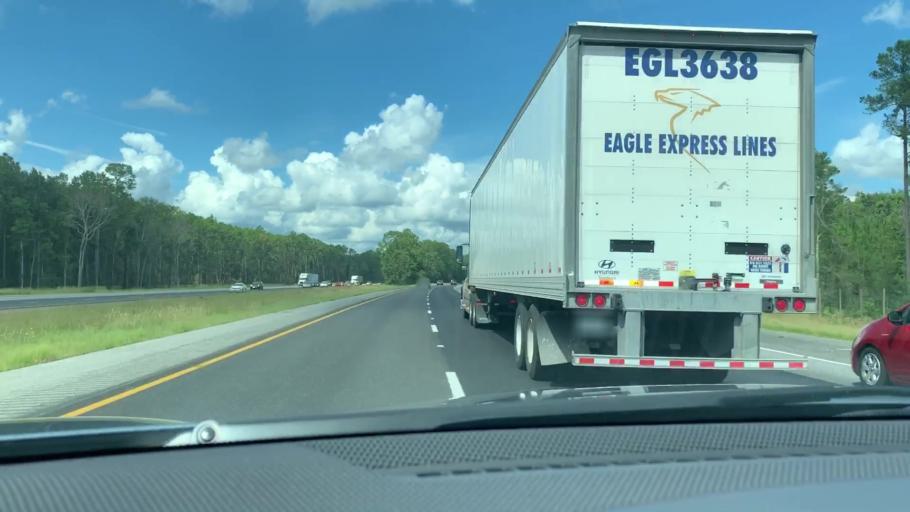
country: US
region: Georgia
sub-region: Camden County
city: Kingsland
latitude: 30.8746
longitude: -81.6849
